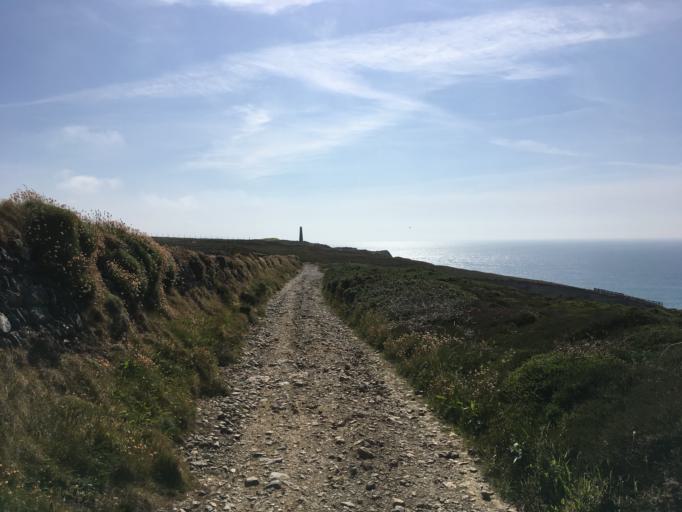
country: GB
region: England
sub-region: Cornwall
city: Redruth
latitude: 50.2810
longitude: -5.2508
